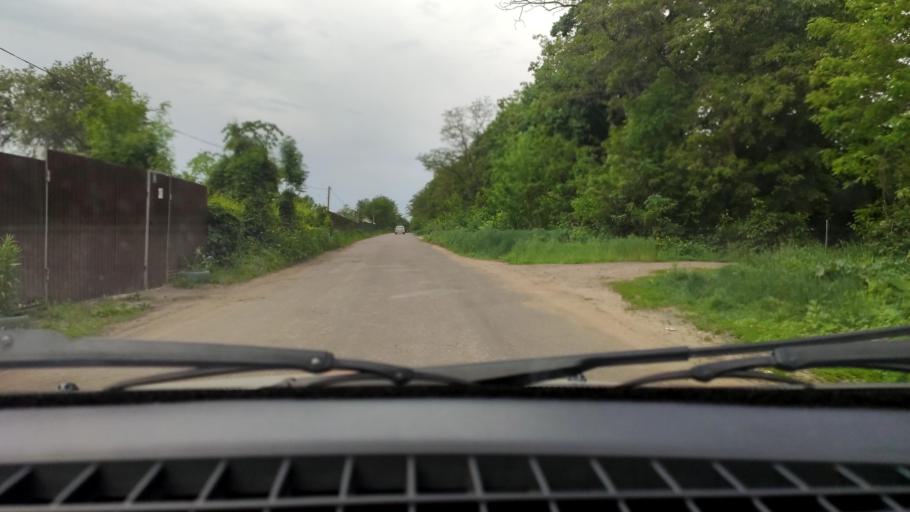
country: RU
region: Voronezj
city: Shilovo
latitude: 51.5980
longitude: 39.1306
